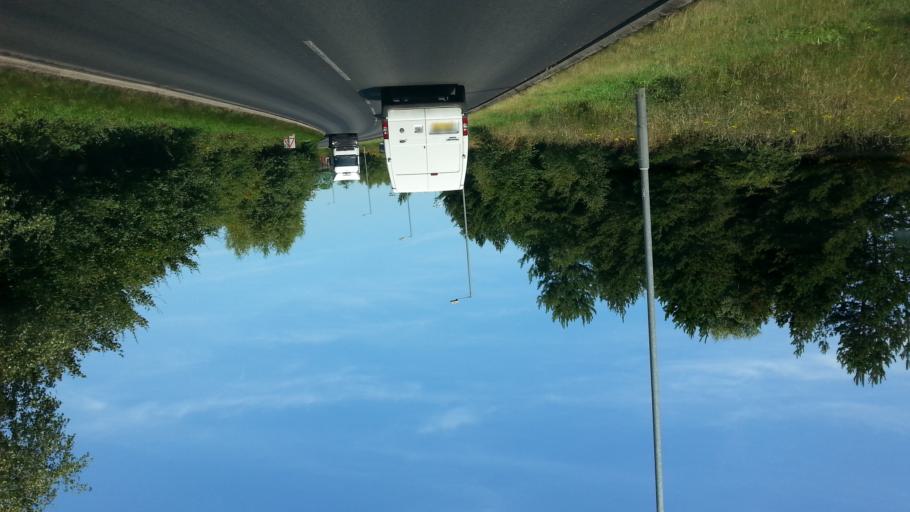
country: GB
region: England
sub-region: Staffordshire
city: Chasetown
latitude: 52.6696
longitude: -1.9417
